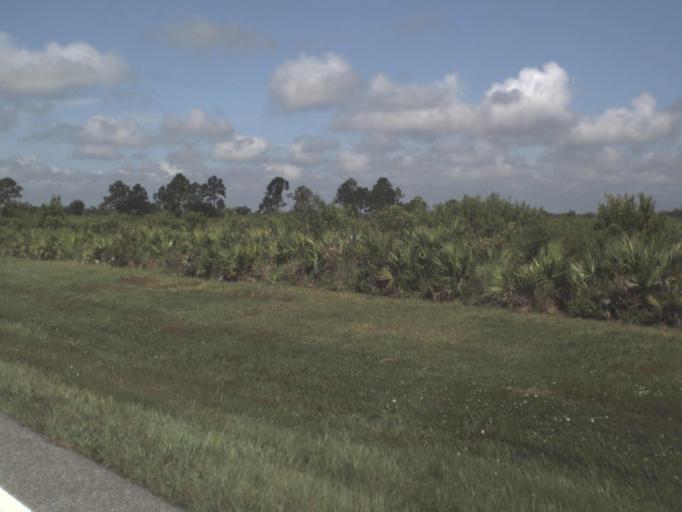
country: US
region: Florida
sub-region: Sarasota County
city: Lake Sarasota
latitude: 27.2219
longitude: -82.2931
